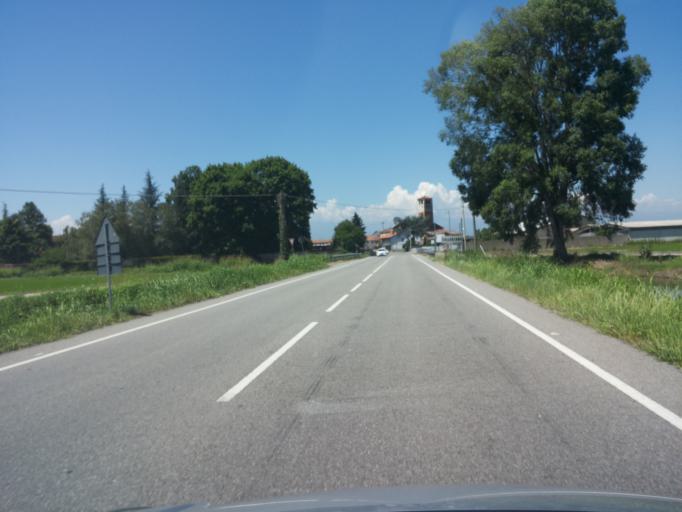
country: IT
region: Piedmont
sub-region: Provincia di Vercelli
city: Collobiano
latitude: 45.3951
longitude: 8.3510
